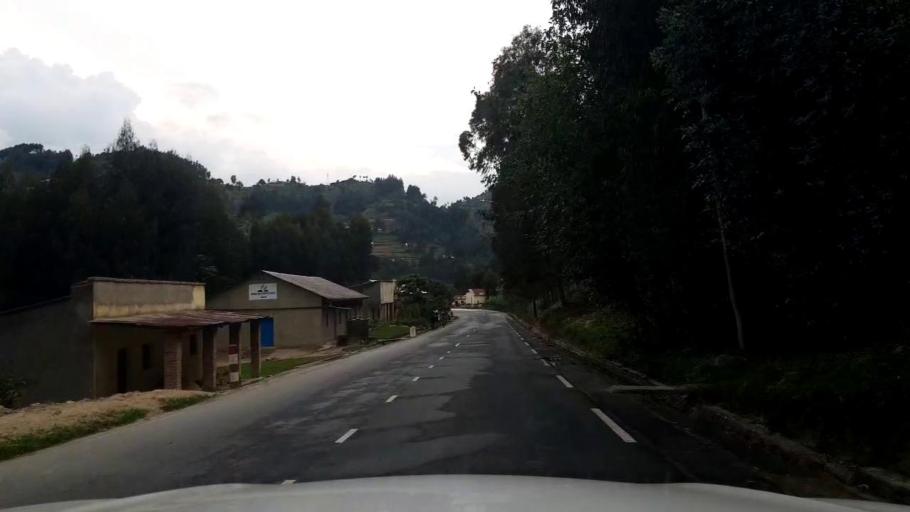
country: RW
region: Northern Province
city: Musanze
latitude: -1.6850
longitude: 29.5168
